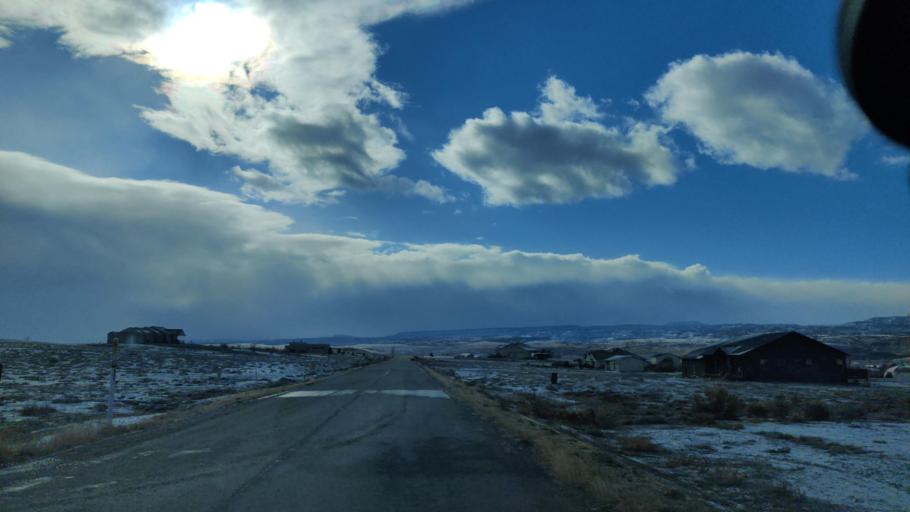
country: US
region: Colorado
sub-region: Mesa County
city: Clifton
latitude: 38.9999
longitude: -108.4247
